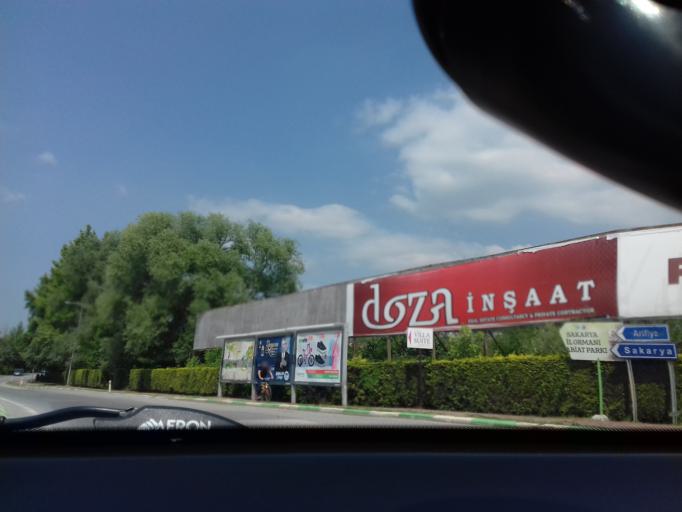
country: TR
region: Sakarya
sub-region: Merkez
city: Sapanca
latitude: 40.6884
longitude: 30.2801
